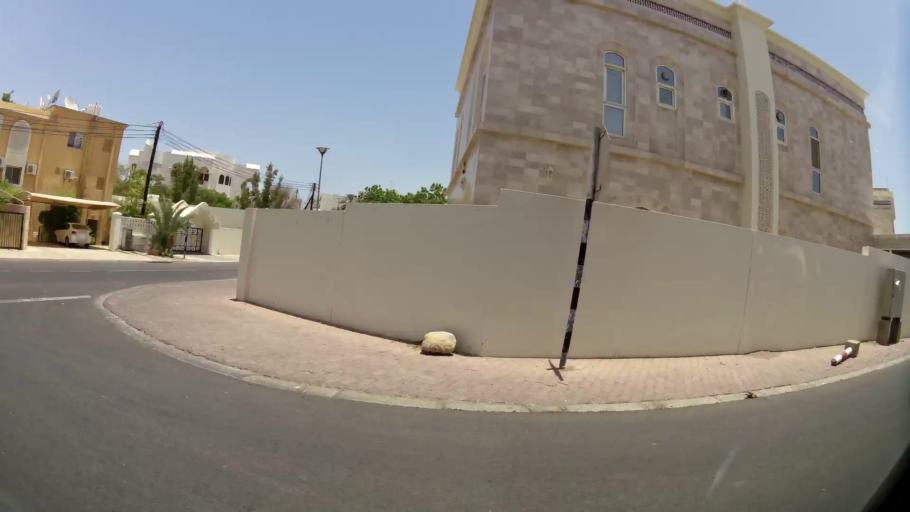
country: OM
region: Muhafazat Masqat
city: Bawshar
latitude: 23.6044
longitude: 58.4606
